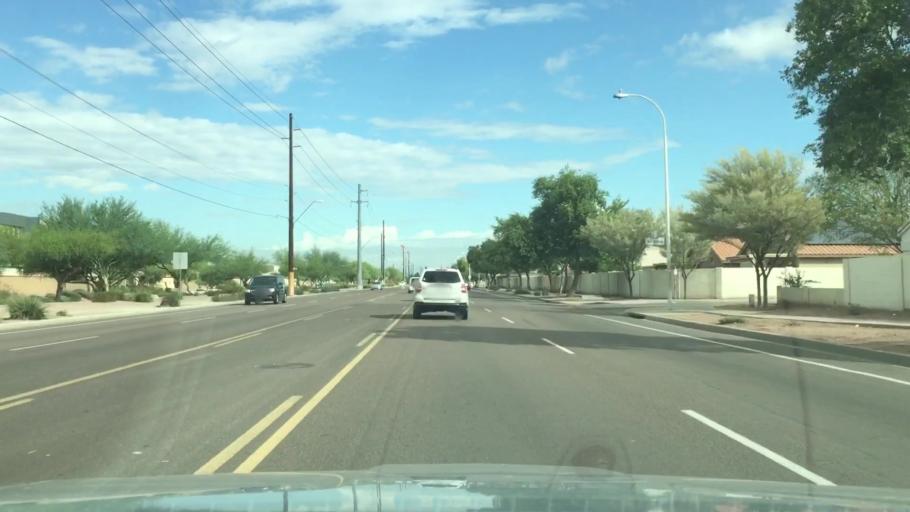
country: US
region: Arizona
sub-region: Maricopa County
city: Tolleson
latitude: 33.4741
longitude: -112.2552
